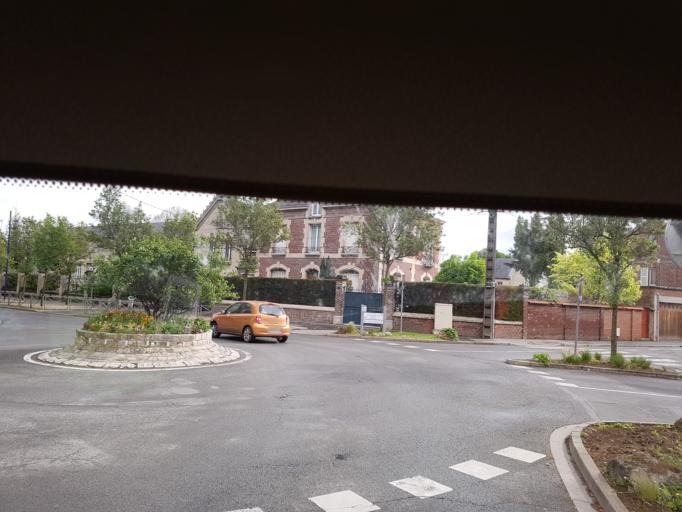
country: FR
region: Picardie
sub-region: Departement de l'Aisne
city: Soissons
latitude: 49.3826
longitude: 3.3357
